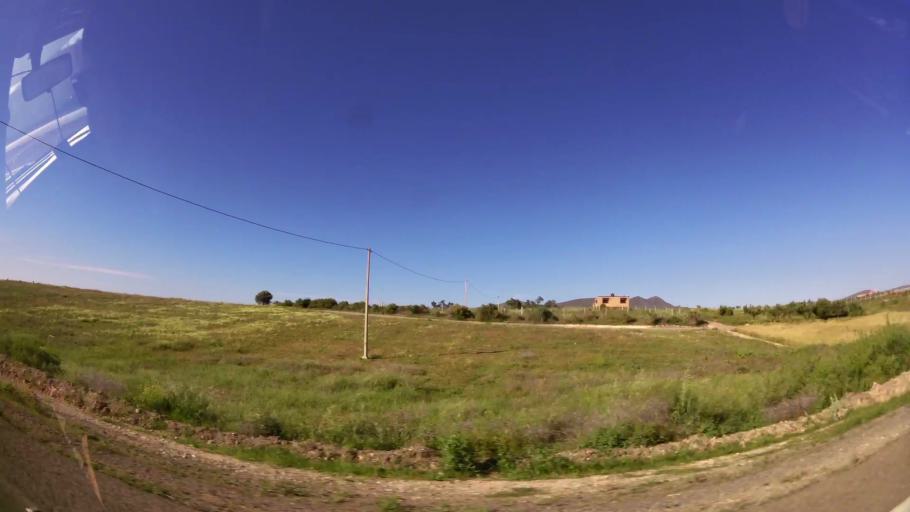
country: MA
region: Oriental
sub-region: Berkane-Taourirt
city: Ahfir
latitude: 34.9788
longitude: -2.1353
